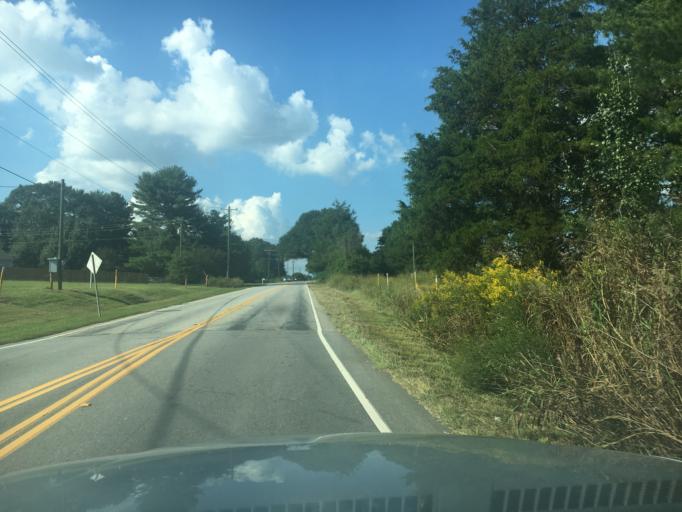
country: US
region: South Carolina
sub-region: Greenville County
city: Simpsonville
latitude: 34.6889
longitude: -82.2523
